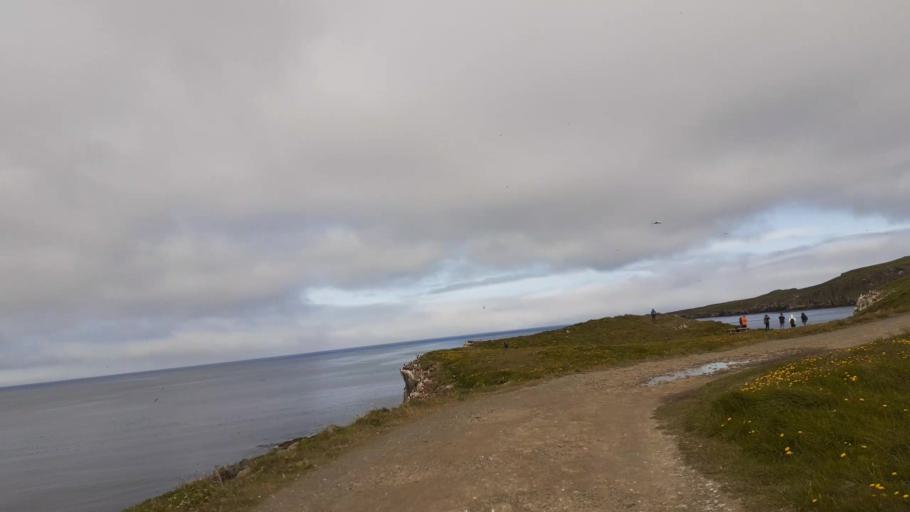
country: IS
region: Northeast
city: Dalvik
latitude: 66.5505
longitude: -18.0253
